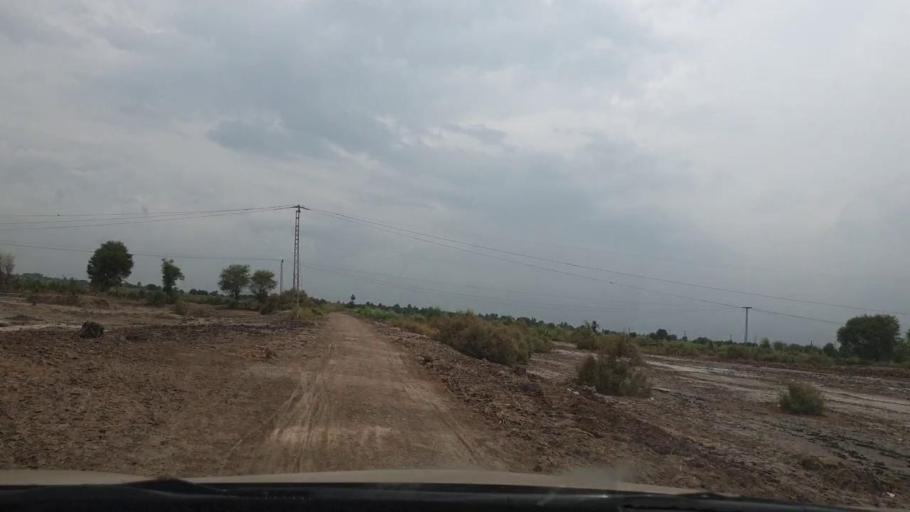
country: PK
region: Sindh
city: Ratodero
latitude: 27.8035
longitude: 68.3136
